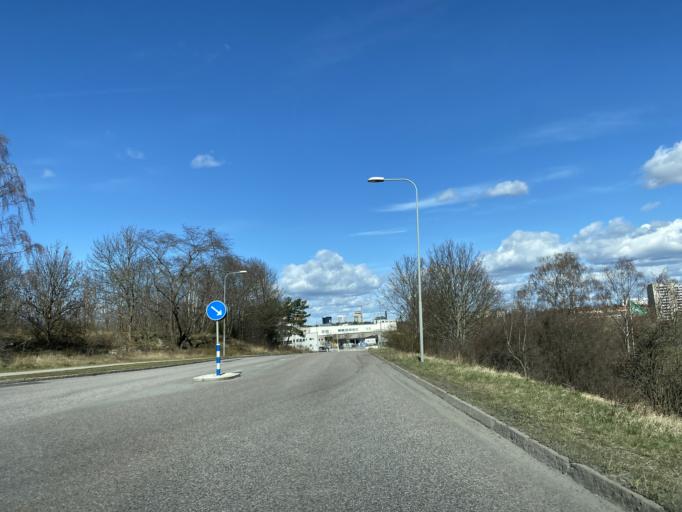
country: SE
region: Stockholm
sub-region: Stockholms Kommun
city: Arsta
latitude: 59.2905
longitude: 18.0373
